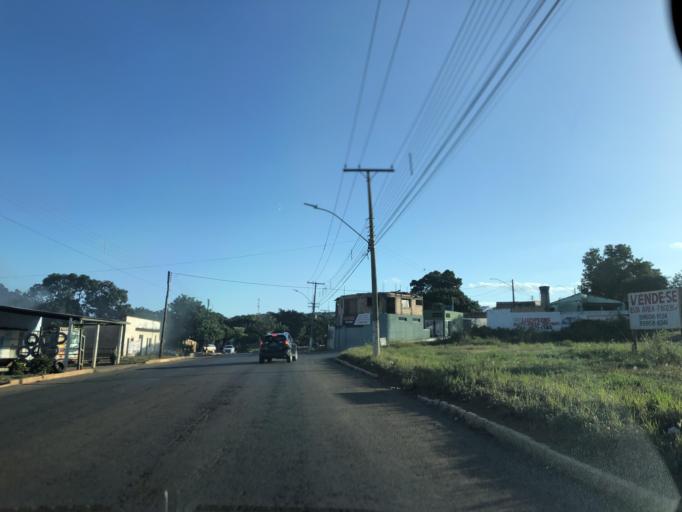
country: BR
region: Goias
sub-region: Luziania
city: Luziania
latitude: -16.2599
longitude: -47.9525
